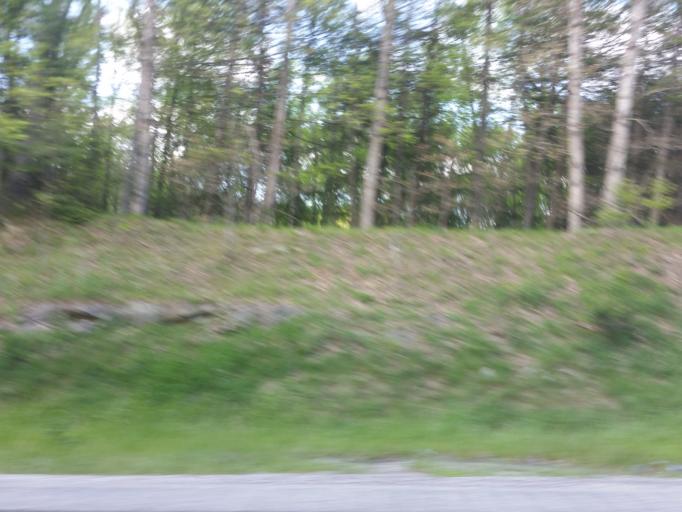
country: US
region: West Virginia
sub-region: Raleigh County
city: Beaver
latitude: 37.7038
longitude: -81.1499
